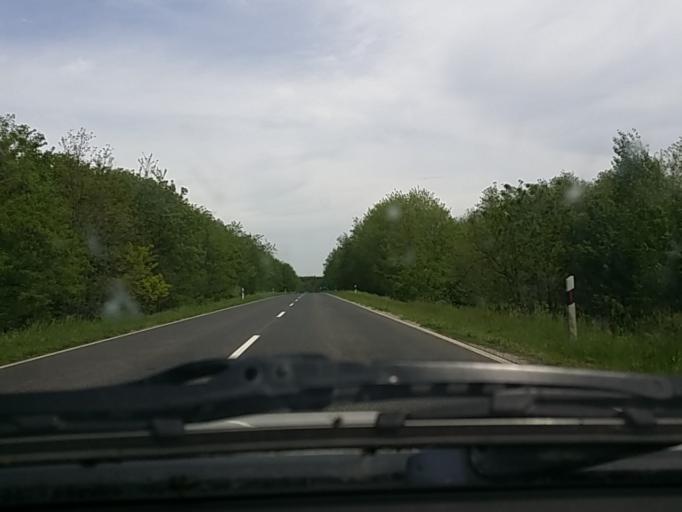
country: HU
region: Somogy
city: Barcs
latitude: 45.9608
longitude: 17.4918
